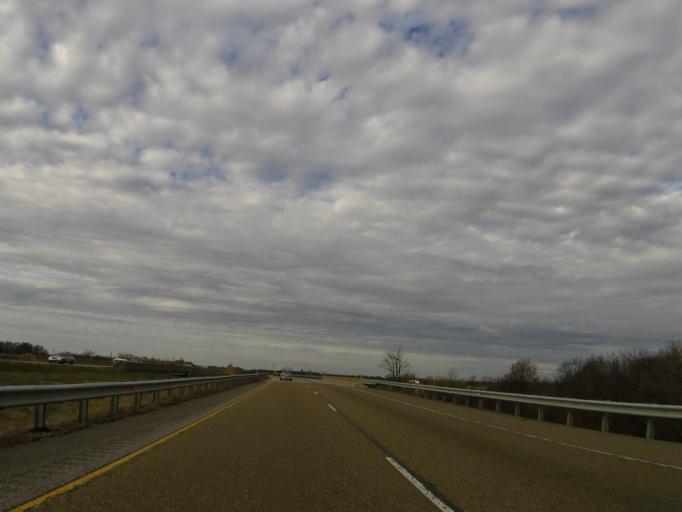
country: US
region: Illinois
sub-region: Clinton County
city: Wamac
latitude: 38.3902
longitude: -89.1759
